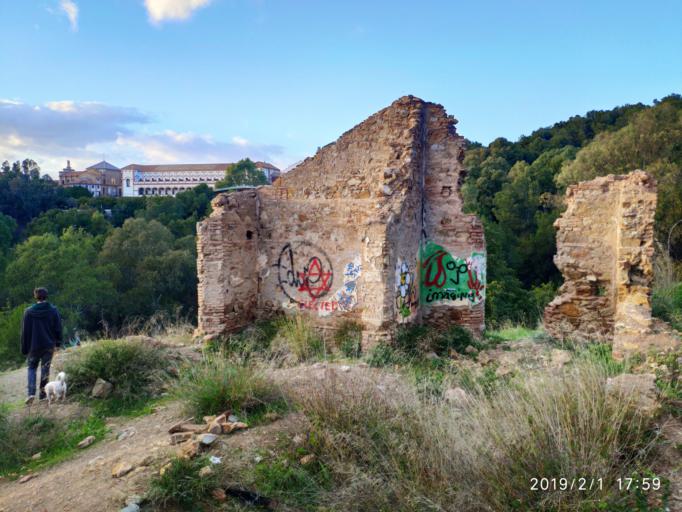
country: ES
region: Andalusia
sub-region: Provincia de Malaga
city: Malaga
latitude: 36.7325
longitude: -4.4090
